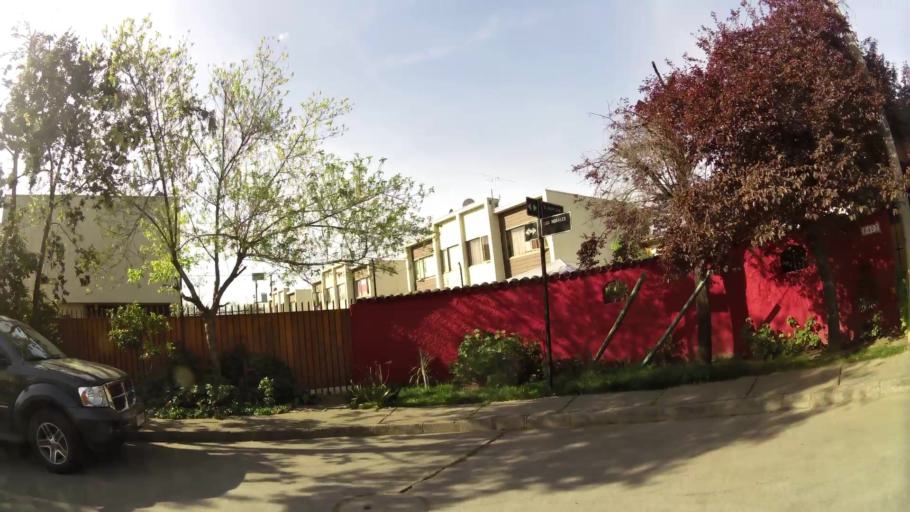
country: CL
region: Santiago Metropolitan
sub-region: Provincia de Santiago
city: Villa Presidente Frei, Nunoa, Santiago, Chile
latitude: -33.5307
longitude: -70.5865
